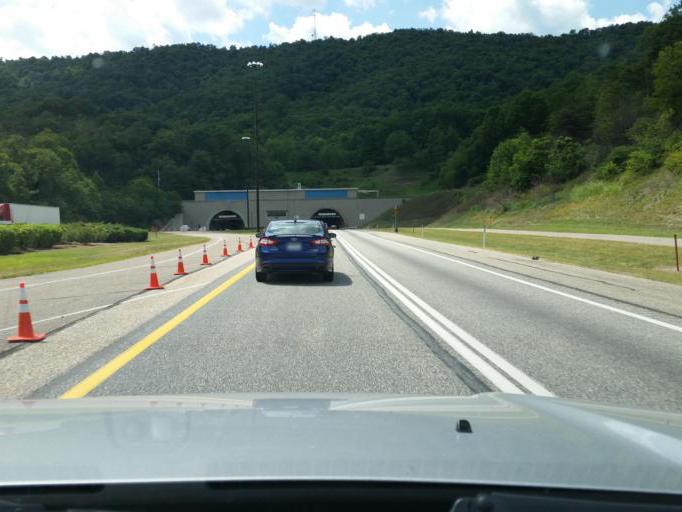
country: US
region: Pennsylvania
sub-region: Franklin County
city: Doylestown
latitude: 40.0871
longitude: -77.8324
